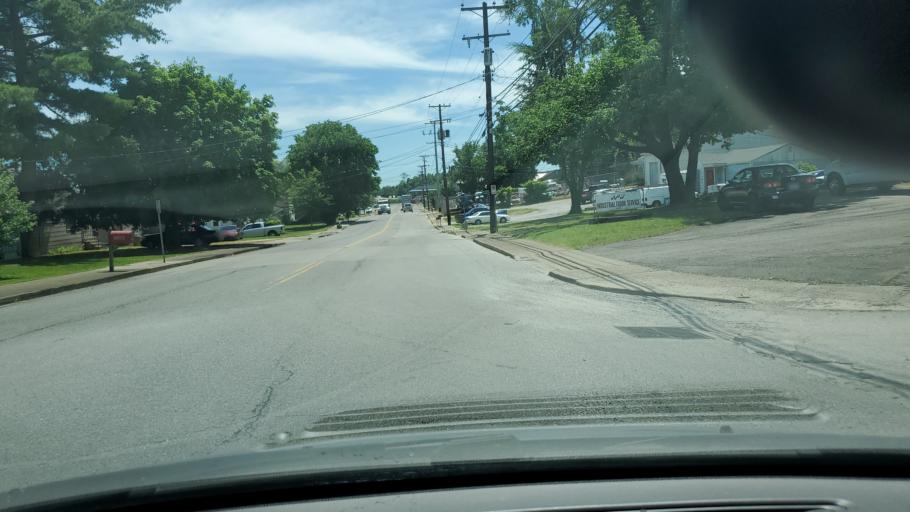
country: US
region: Tennessee
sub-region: Davidson County
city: Nashville
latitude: 36.2071
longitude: -86.7481
